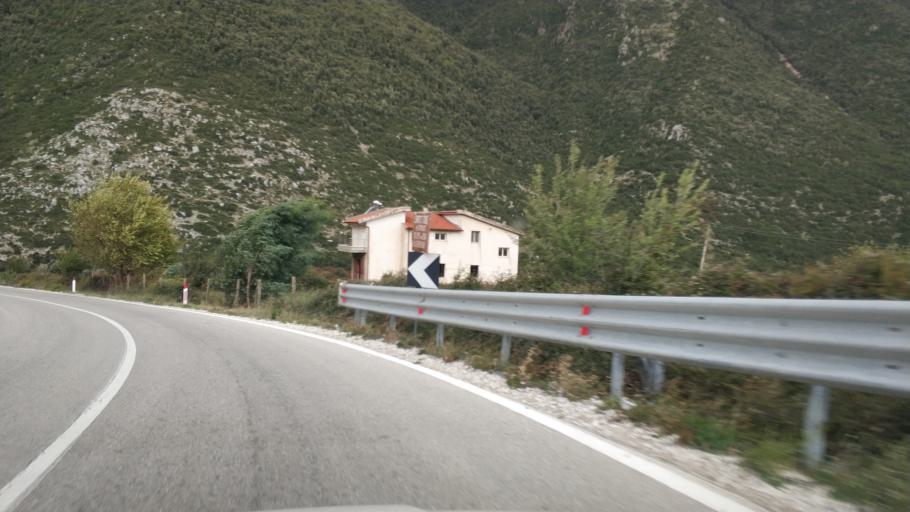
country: AL
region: Vlore
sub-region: Rrethi i Vlores
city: Brataj
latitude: 40.2351
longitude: 19.5596
